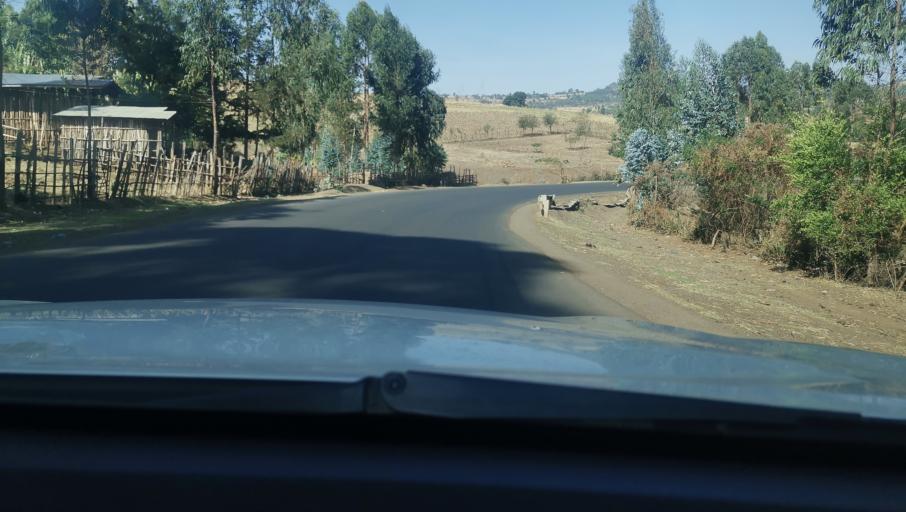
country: ET
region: Oromiya
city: Gedo
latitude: 8.9682
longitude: 37.5201
